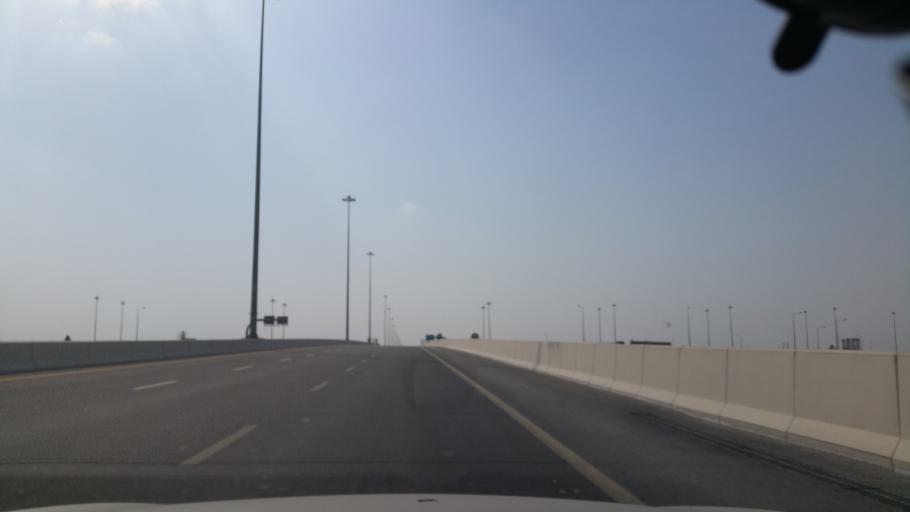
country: QA
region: Baladiyat Umm Salal
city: Umm Salal `Ali
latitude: 25.4570
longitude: 51.4815
